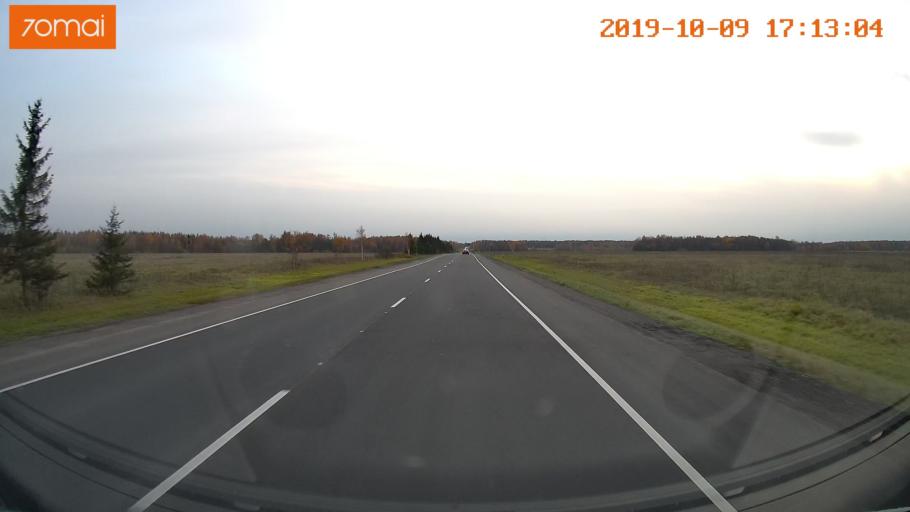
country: RU
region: Ivanovo
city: Privolzhsk
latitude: 57.3198
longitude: 41.2303
